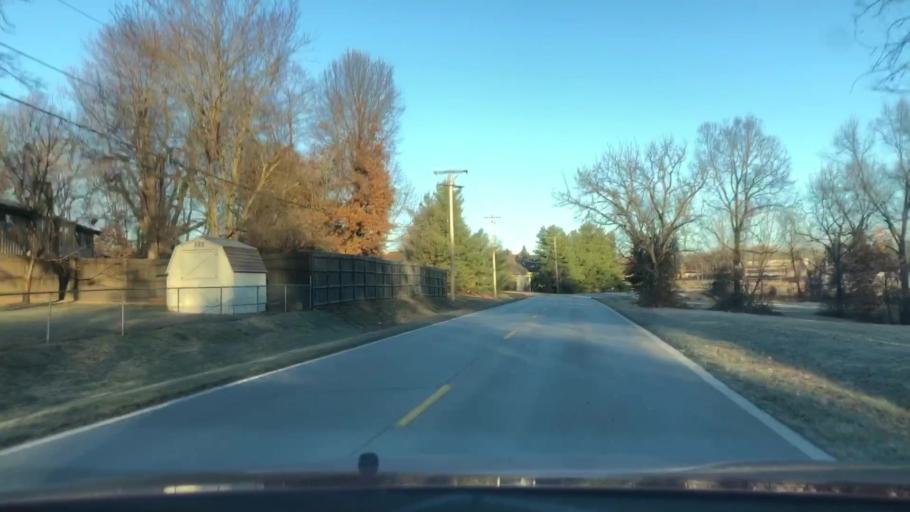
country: US
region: Missouri
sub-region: Greene County
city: Springfield
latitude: 37.1654
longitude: -93.2456
